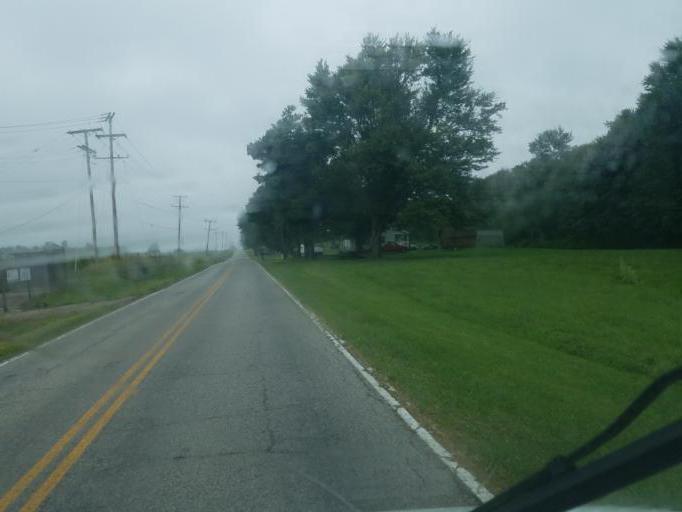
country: US
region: Ohio
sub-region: Knox County
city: Centerburg
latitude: 40.2501
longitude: -82.6922
